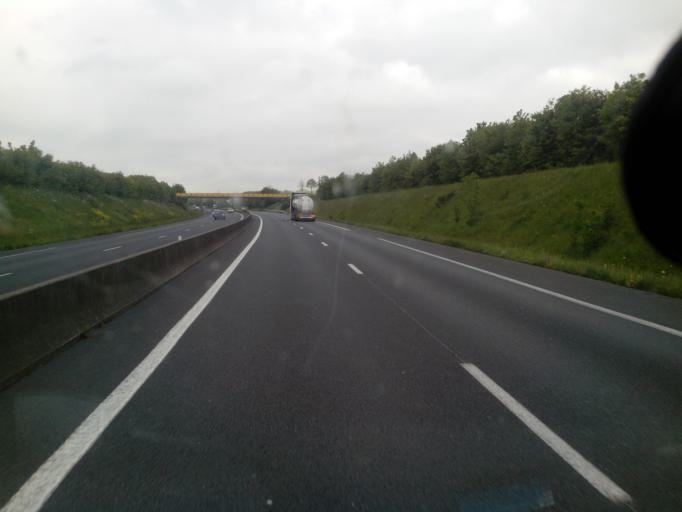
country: FR
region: Lower Normandy
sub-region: Departement du Calvados
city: Villers-Bocage
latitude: 49.0758
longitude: -0.6428
